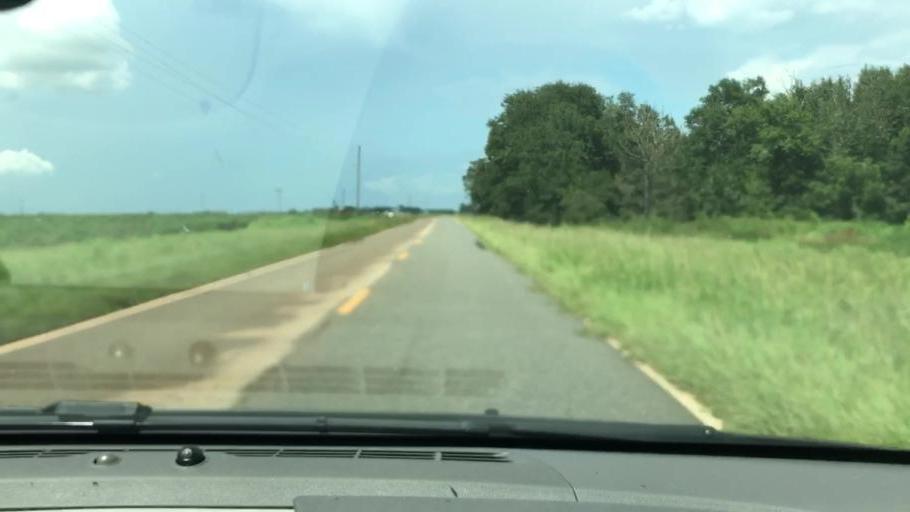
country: US
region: Georgia
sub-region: Seminole County
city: Donalsonville
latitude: 31.0963
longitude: -84.9962
